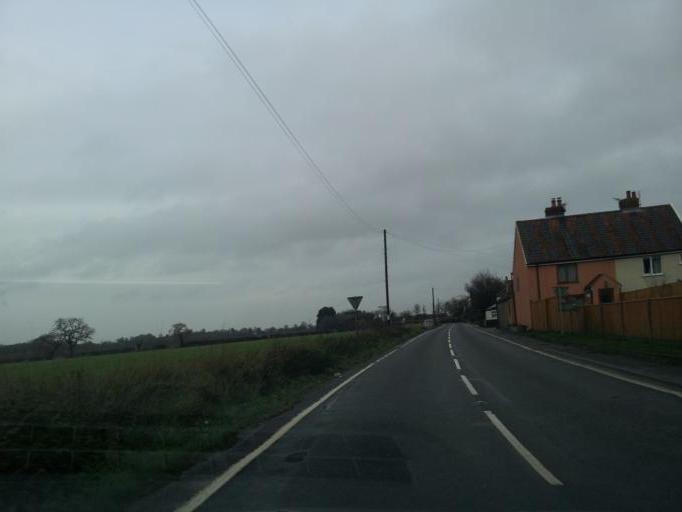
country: GB
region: England
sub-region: Norfolk
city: Acle
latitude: 52.6610
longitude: 1.5842
